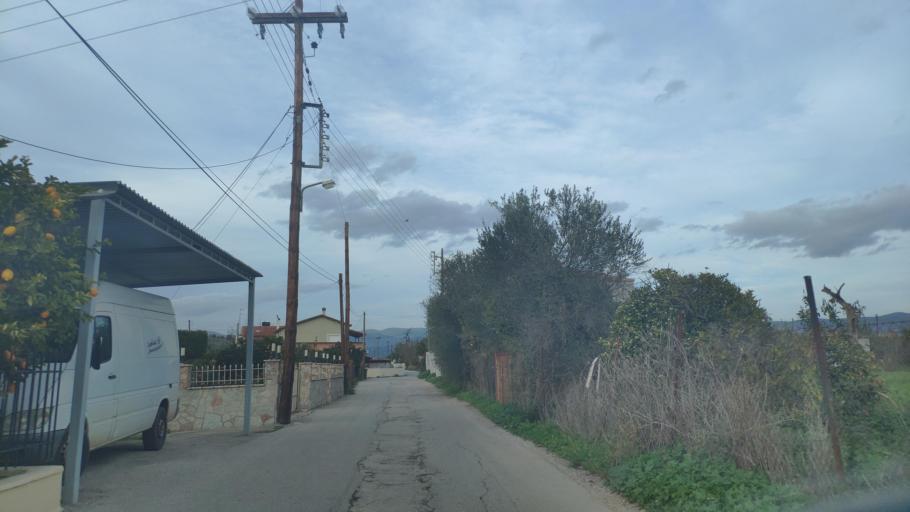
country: GR
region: Peloponnese
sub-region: Nomos Argolidos
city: Nea Tirins
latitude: 37.6053
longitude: 22.8108
